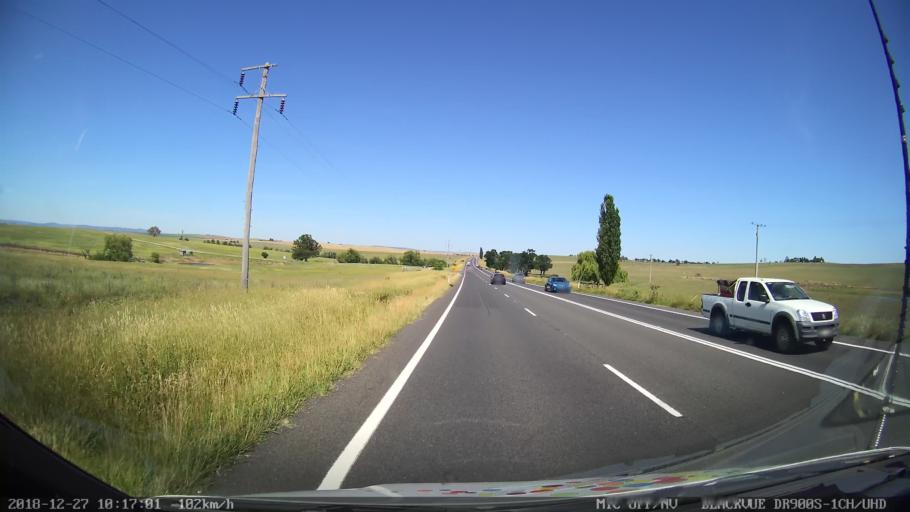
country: AU
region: New South Wales
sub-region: Bathurst Regional
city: Kelso
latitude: -33.4260
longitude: 149.6856
